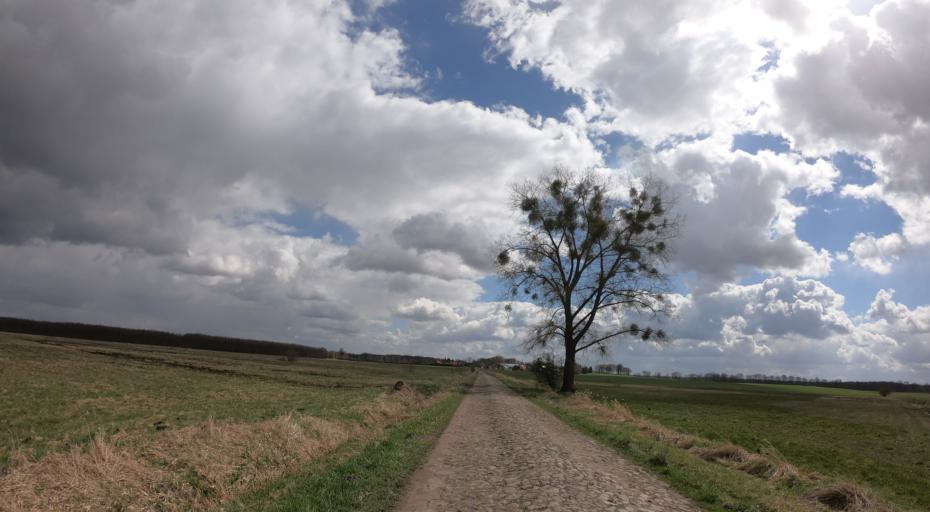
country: PL
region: West Pomeranian Voivodeship
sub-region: Powiat drawski
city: Drawsko Pomorskie
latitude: 53.5454
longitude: 15.8633
